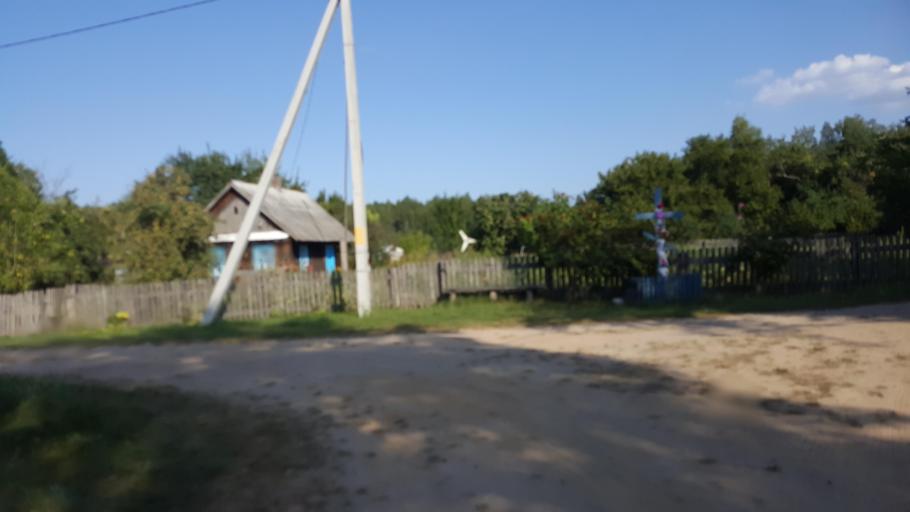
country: BY
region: Brest
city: Kamyanyuki
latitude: 52.5614
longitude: 23.6401
